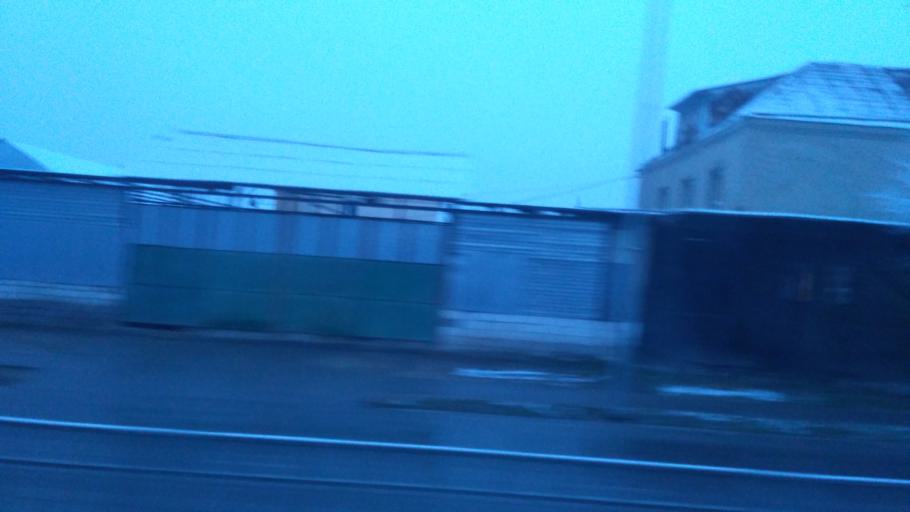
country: KZ
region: Ongtustik Qazaqstan
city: Shymkent
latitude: 42.3750
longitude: 69.5009
